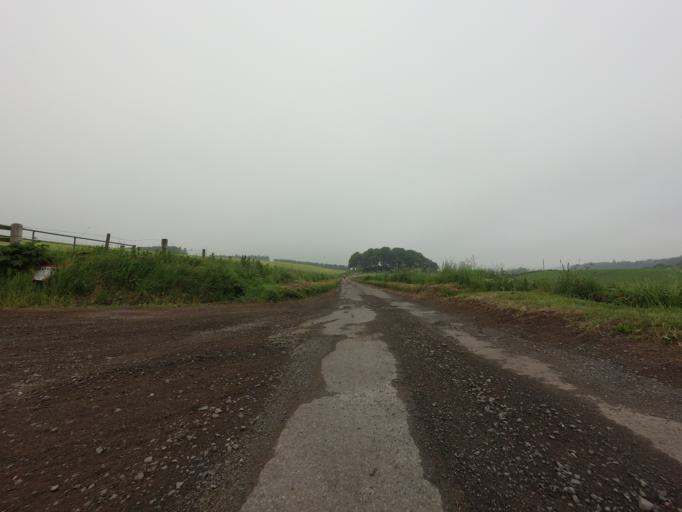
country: GB
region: Scotland
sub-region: Fife
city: Auchtermuchty
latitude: 56.2703
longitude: -3.2876
